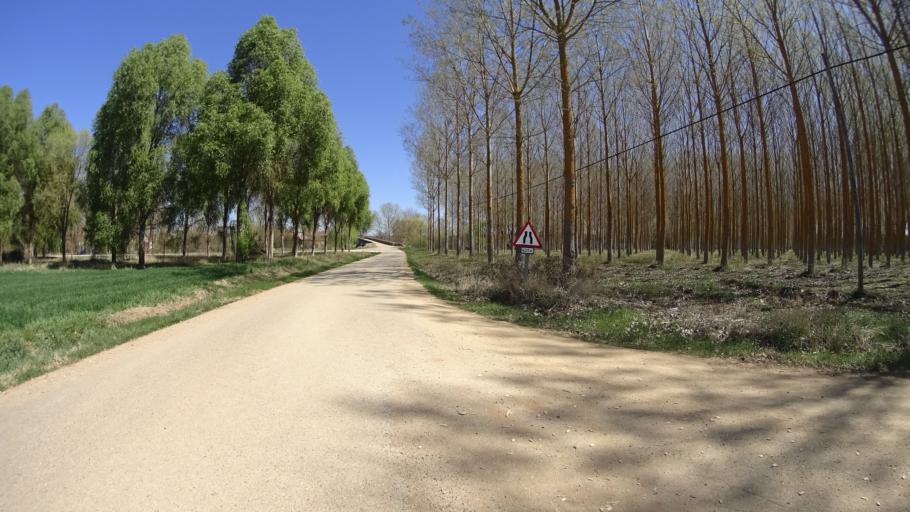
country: ES
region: Castille and Leon
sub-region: Provincia de Burgos
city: Rezmondo
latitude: 42.5332
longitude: -4.2712
